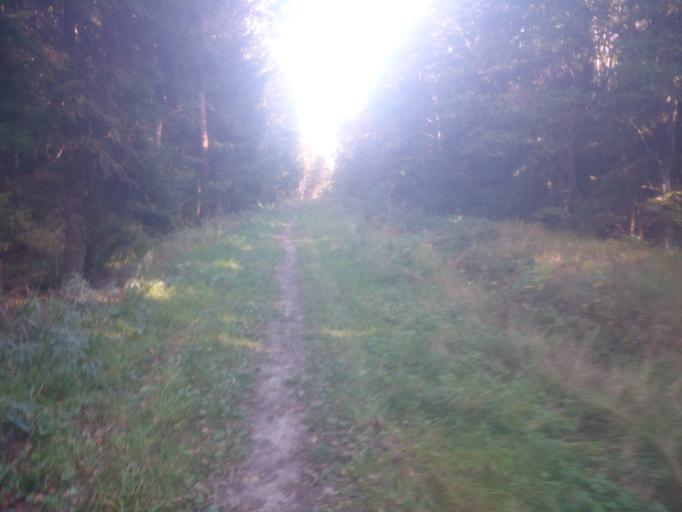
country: SE
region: Stockholm
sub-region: Upplands-Bro Kommun
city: Kungsaengen
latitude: 59.4974
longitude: 17.7377
